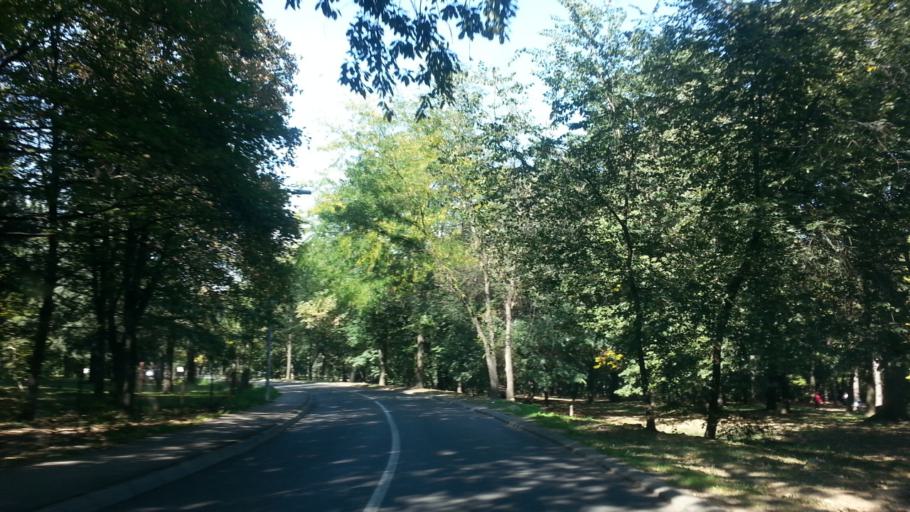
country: RS
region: Central Serbia
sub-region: Belgrade
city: Cukarica
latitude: 44.7718
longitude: 20.4253
